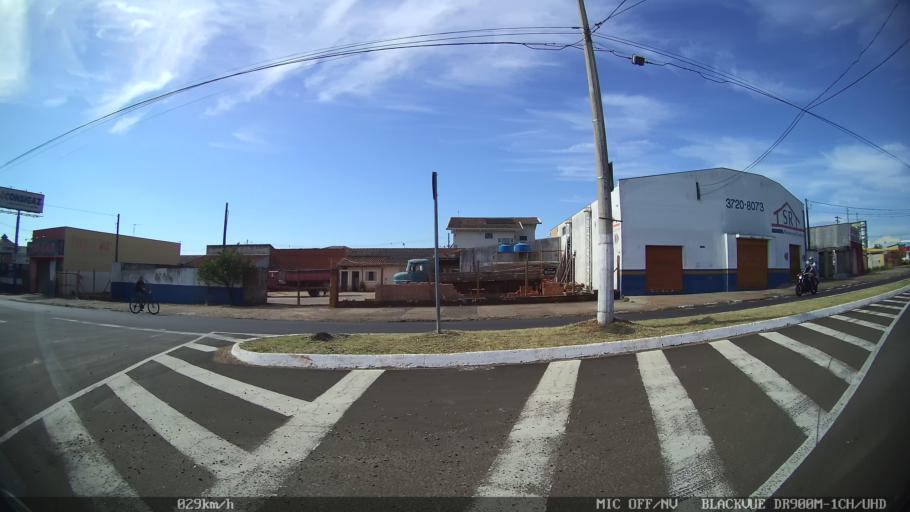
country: BR
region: Sao Paulo
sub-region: Franca
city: Franca
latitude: -20.5267
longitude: -47.4315
